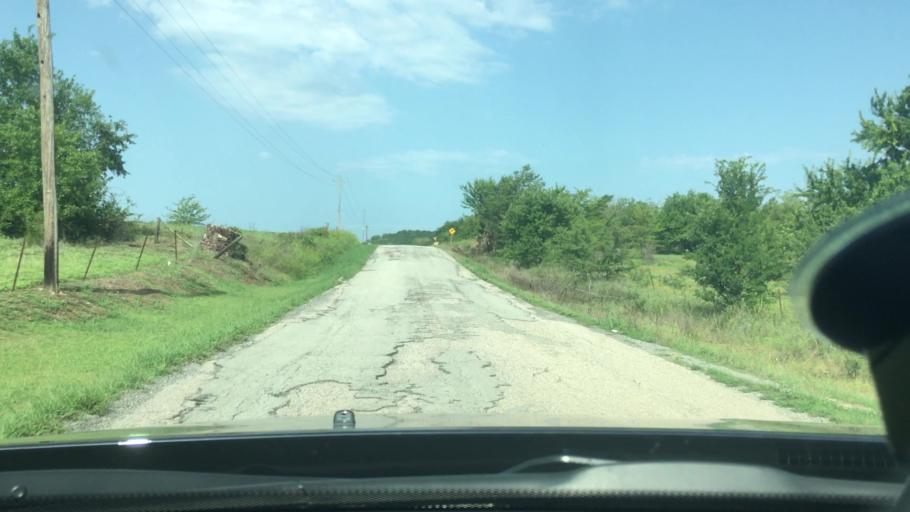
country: US
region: Oklahoma
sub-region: Atoka County
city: Atoka
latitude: 34.4616
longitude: -96.0380
